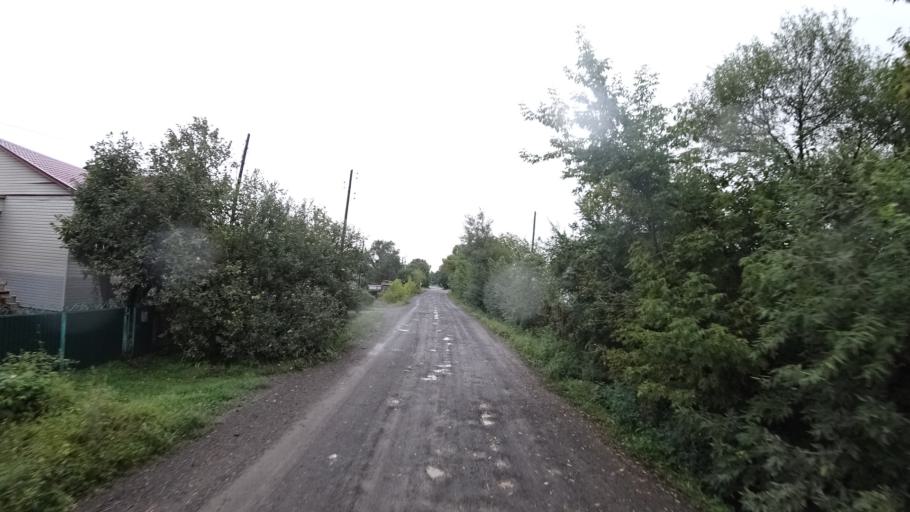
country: RU
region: Primorskiy
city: Chernigovka
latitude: 44.3378
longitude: 132.5712
